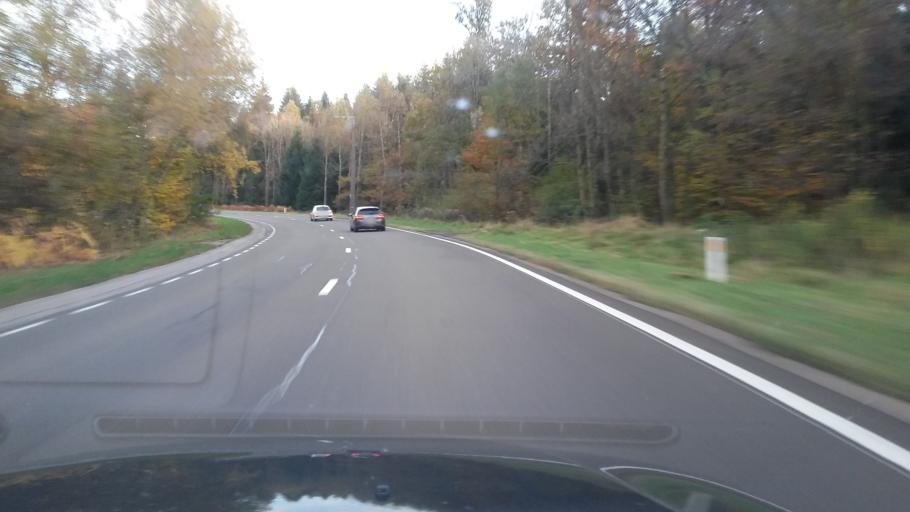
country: BE
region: Wallonia
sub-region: Province du Luxembourg
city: Bouillon
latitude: 49.7593
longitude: 5.1386
